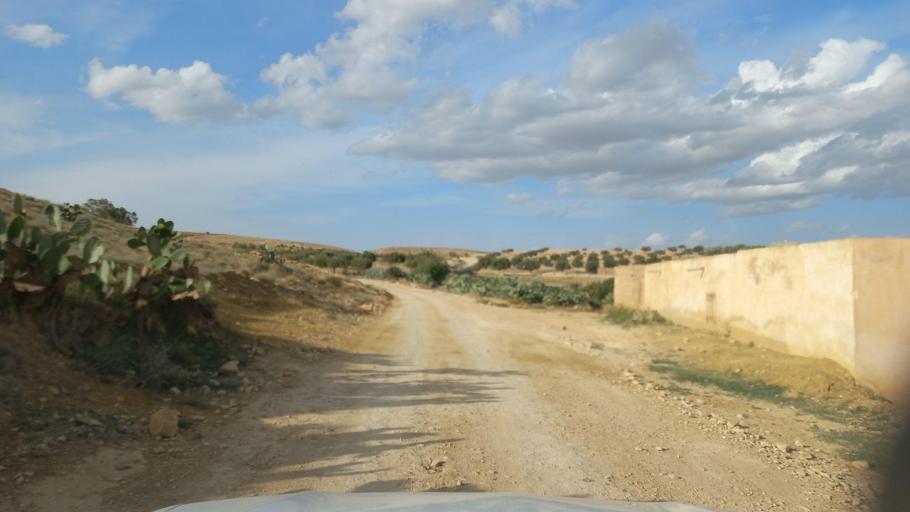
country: TN
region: Al Qasrayn
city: Sbiba
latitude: 35.4526
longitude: 9.0834
